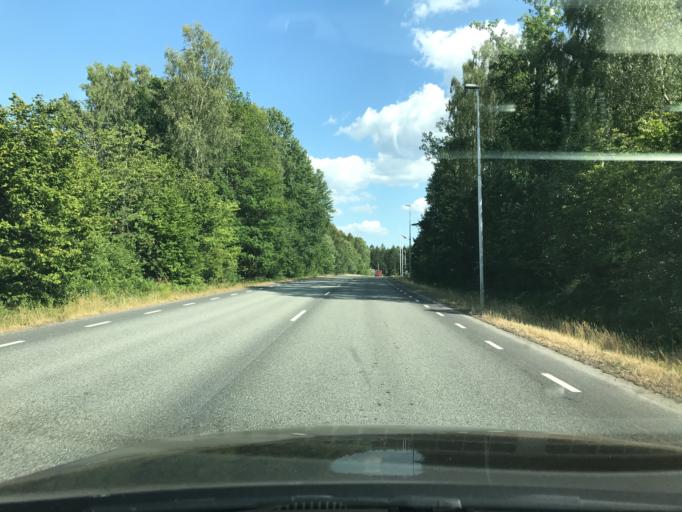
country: SE
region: Skane
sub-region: Hassleholms Kommun
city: Hastveda
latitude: 56.2742
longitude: 13.9500
